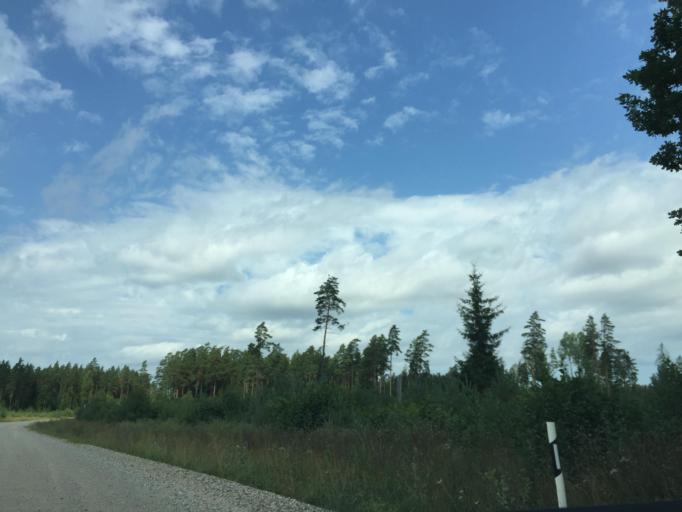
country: LV
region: Kandava
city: Kandava
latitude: 57.0122
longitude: 22.8354
